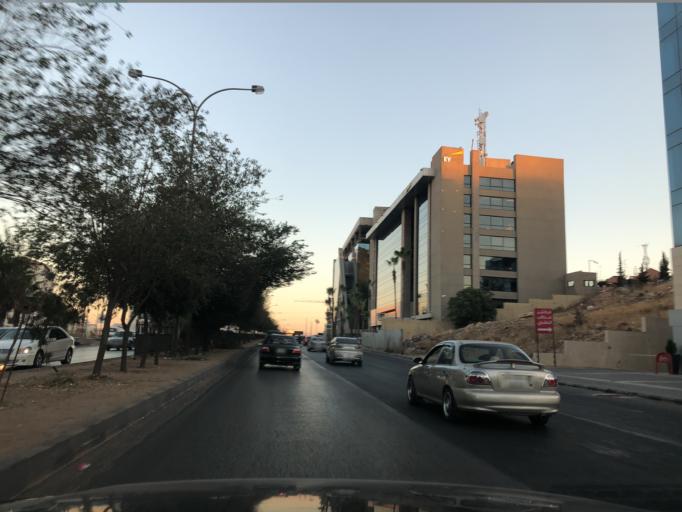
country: JO
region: Amman
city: Wadi as Sir
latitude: 31.9653
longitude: 35.8432
